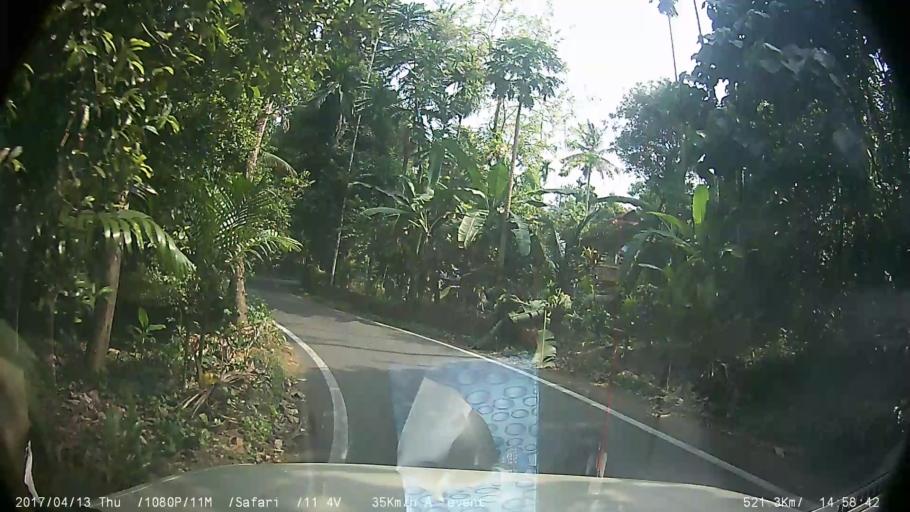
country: IN
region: Kerala
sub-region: Ernakulam
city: Ramamangalam
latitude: 9.9496
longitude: 76.5021
